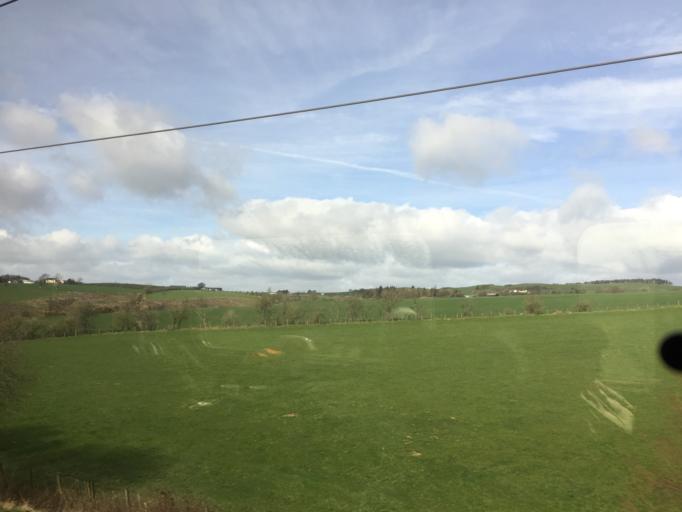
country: GB
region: Scotland
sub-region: Dumfries and Galloway
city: Annan
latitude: 55.0659
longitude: -3.2923
